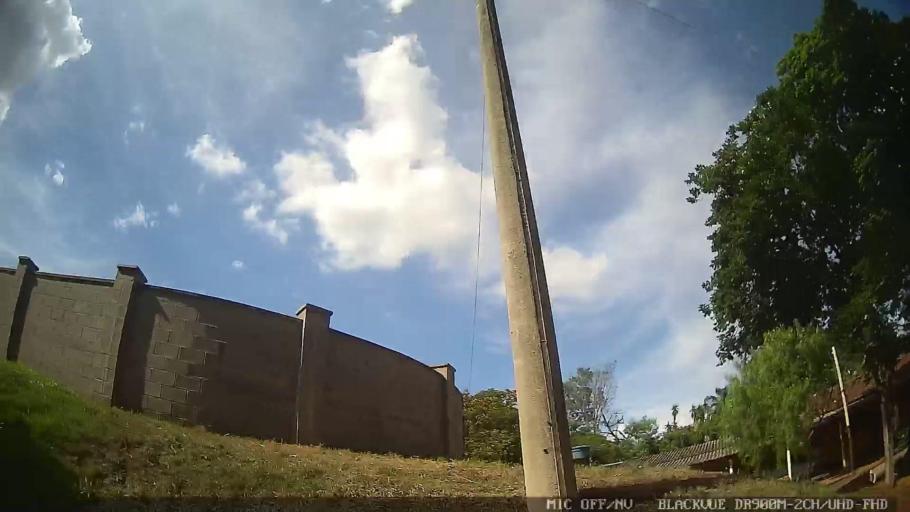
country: BR
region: Sao Paulo
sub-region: Jaguariuna
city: Jaguariuna
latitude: -22.6317
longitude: -47.0731
